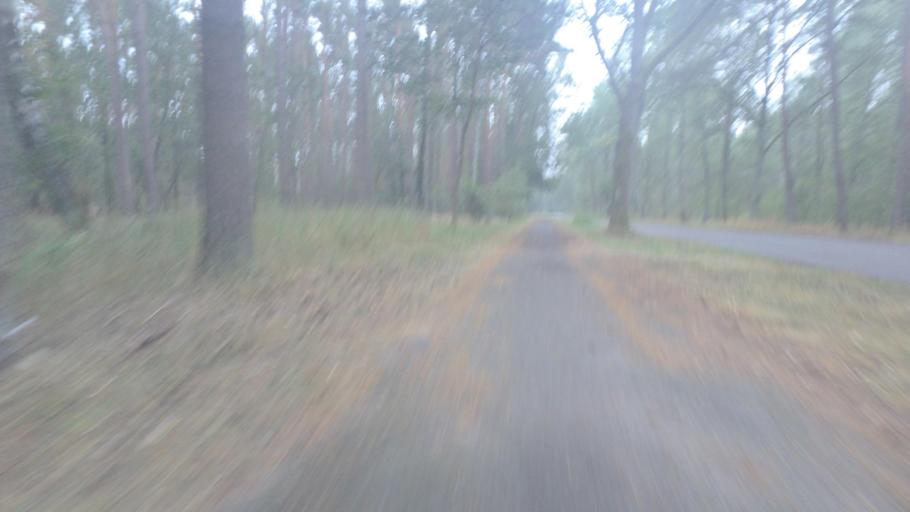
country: DE
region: Brandenburg
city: Heiligengrabe
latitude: 53.1321
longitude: 12.3729
